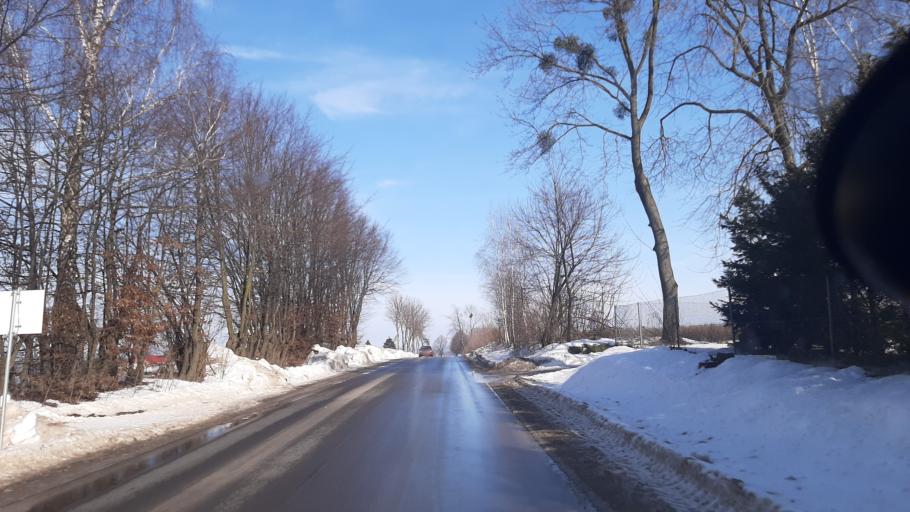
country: PL
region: Lublin Voivodeship
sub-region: Powiat pulawski
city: Kurow
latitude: 51.3597
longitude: 22.1362
